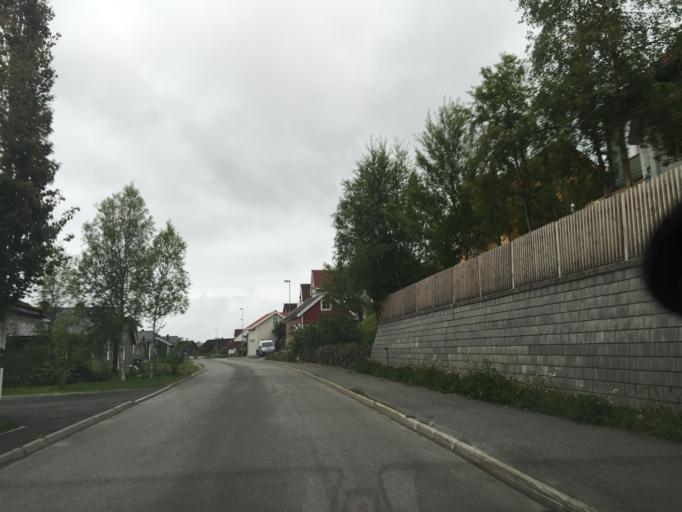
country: NO
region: Nordland
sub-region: Bodo
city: Loding
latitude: 67.2965
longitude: 14.5975
